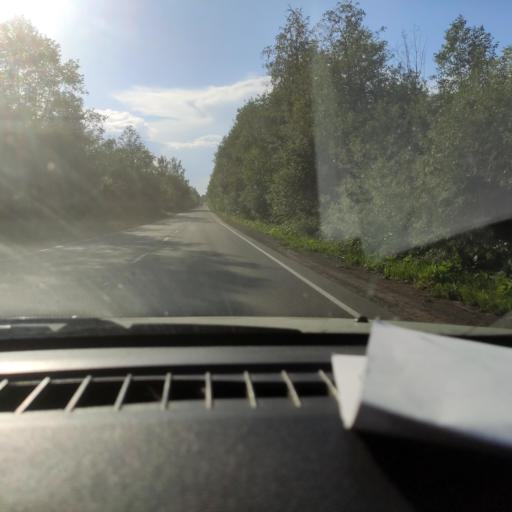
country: RU
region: Perm
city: Krasnokamsk
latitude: 58.1299
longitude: 55.7880
